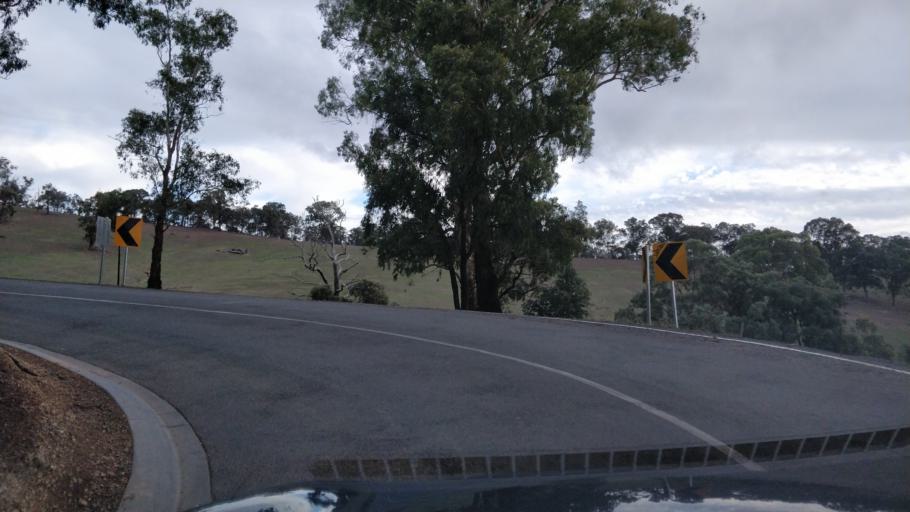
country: AU
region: Victoria
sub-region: Nillumbik
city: Research
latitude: -37.6870
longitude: 145.1763
